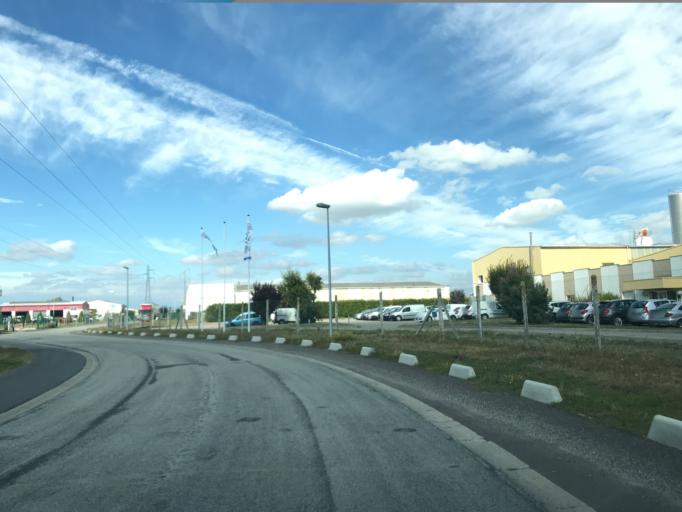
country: FR
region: Haute-Normandie
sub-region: Departement de l'Eure
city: Gaillon
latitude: 49.1653
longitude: 1.3504
